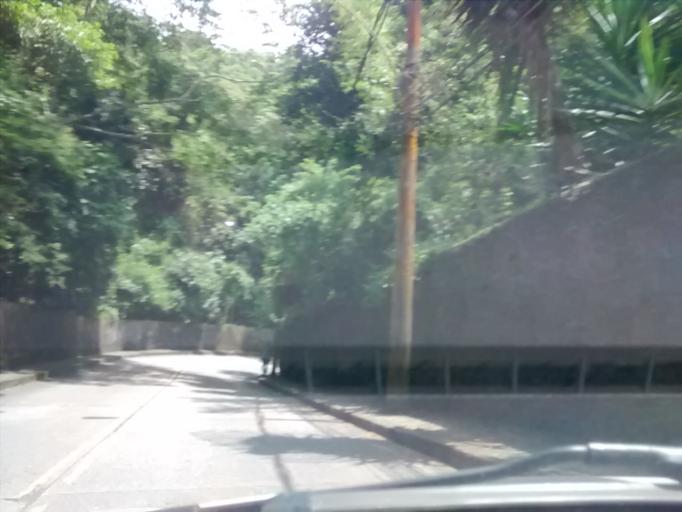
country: BR
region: Rio de Janeiro
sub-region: Rio De Janeiro
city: Rio de Janeiro
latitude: -22.9746
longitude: -43.2808
